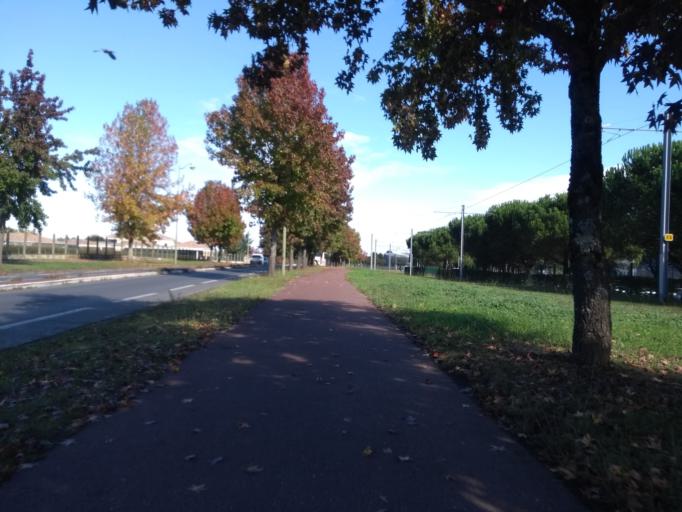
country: FR
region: Aquitaine
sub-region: Departement de la Gironde
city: Gradignan
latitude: 44.7947
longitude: -0.6229
